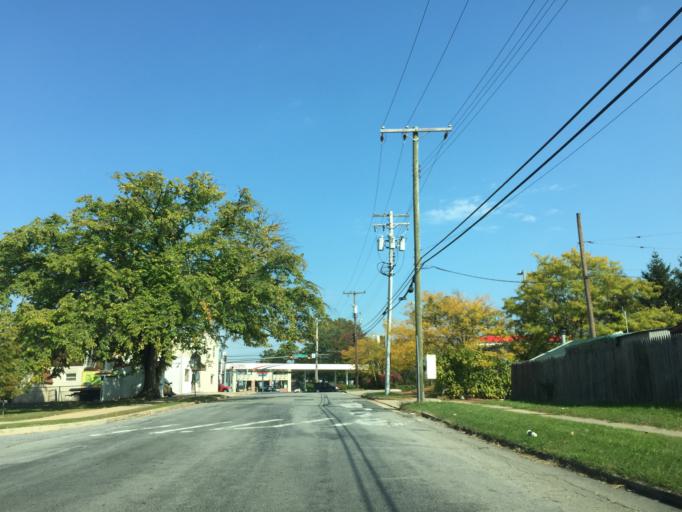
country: US
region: Maryland
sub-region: Baltimore County
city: Middle River
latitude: 39.3124
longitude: -76.4498
